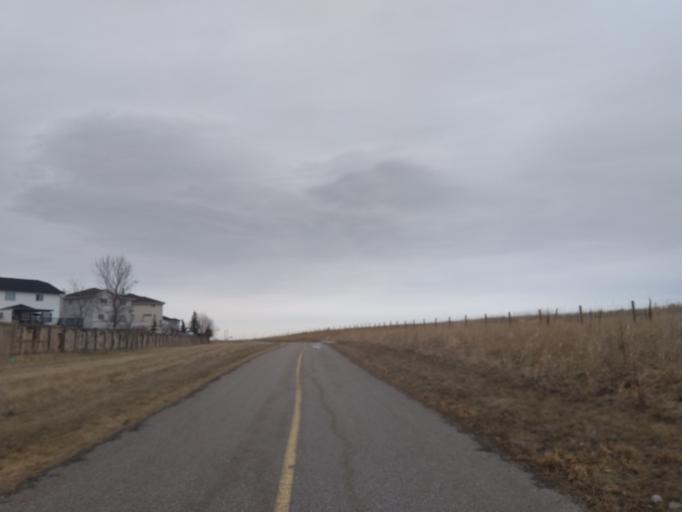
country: CA
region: Alberta
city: Chestermere
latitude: 51.1003
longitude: -113.9230
